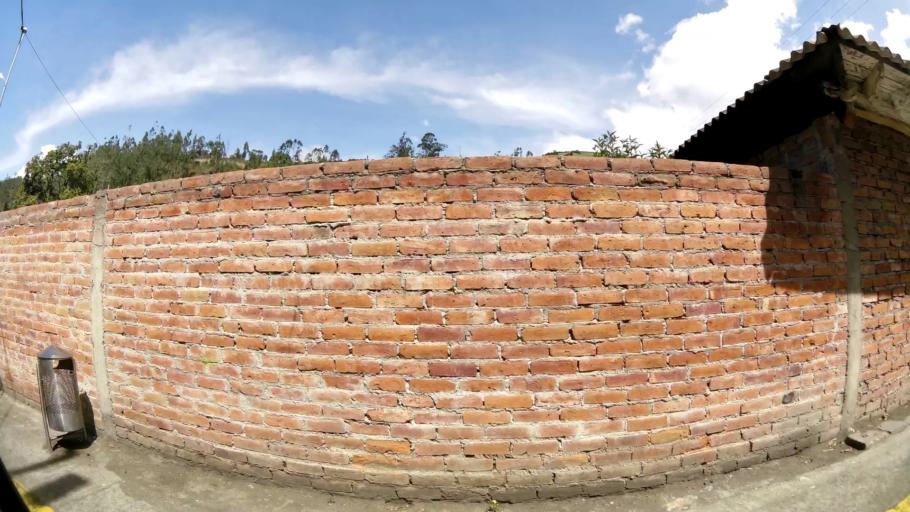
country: EC
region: Chimborazo
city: Guano
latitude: -1.5649
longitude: -78.5311
